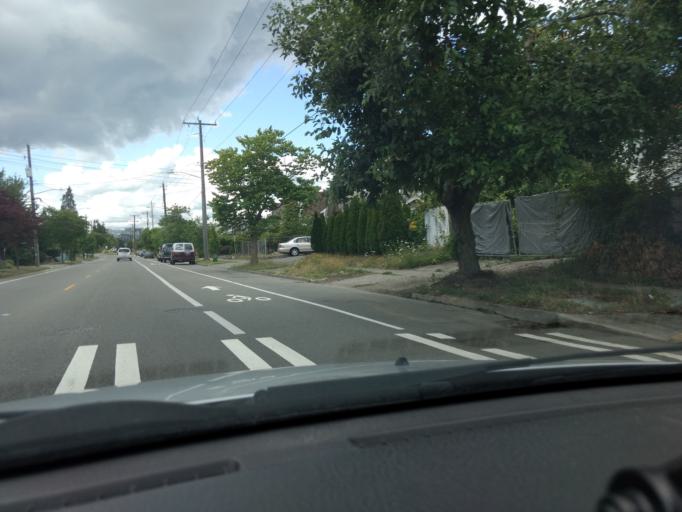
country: US
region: Washington
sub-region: King County
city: Riverton
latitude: 47.5311
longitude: -122.2787
